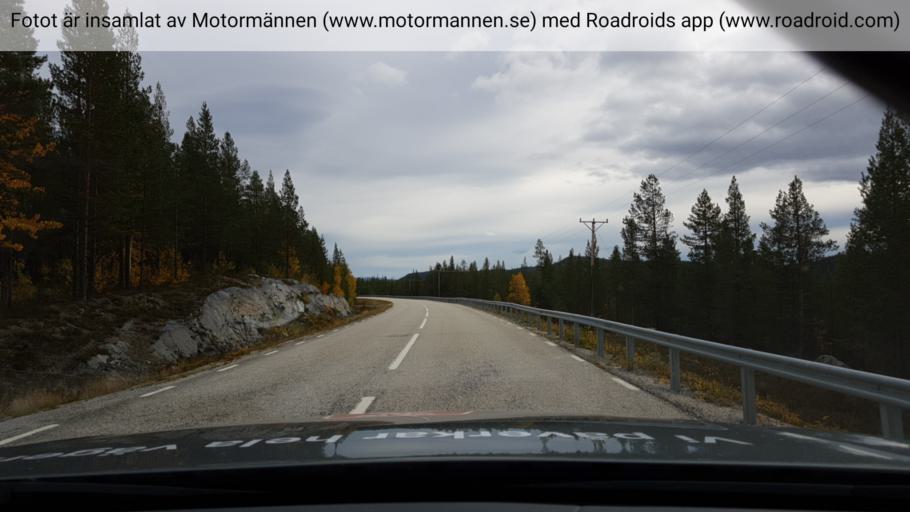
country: SE
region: Jaemtland
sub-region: Are Kommun
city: Jarpen
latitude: 62.7945
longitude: 13.6775
